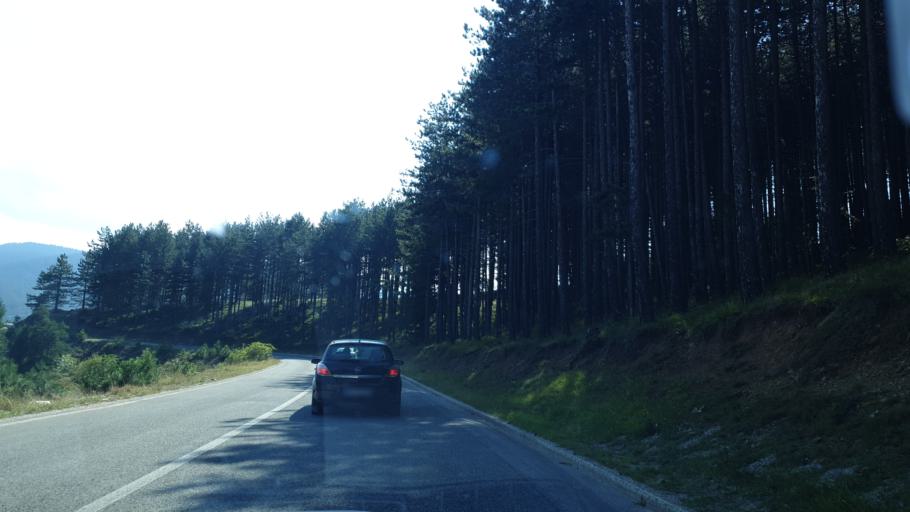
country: RS
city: Zlatibor
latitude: 43.6846
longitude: 19.6543
